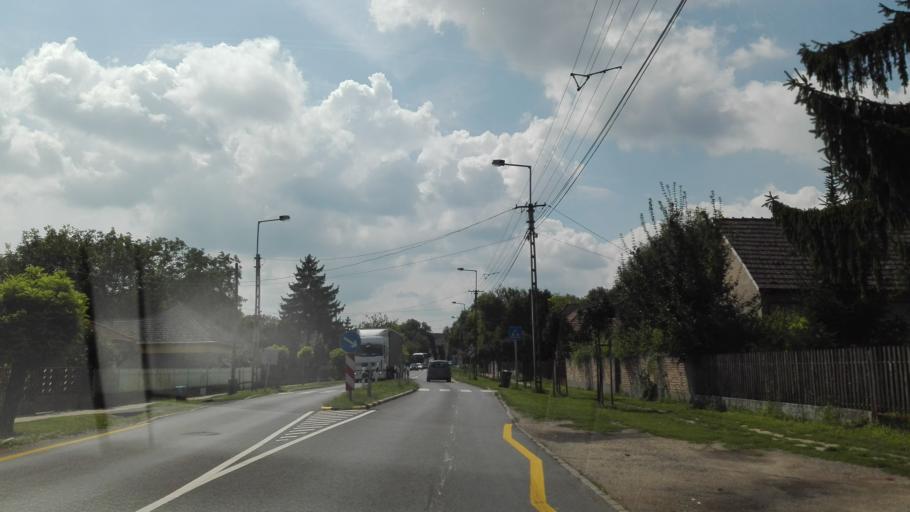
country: HU
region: Fejer
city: Eloszallas
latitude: 46.8316
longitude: 18.8252
